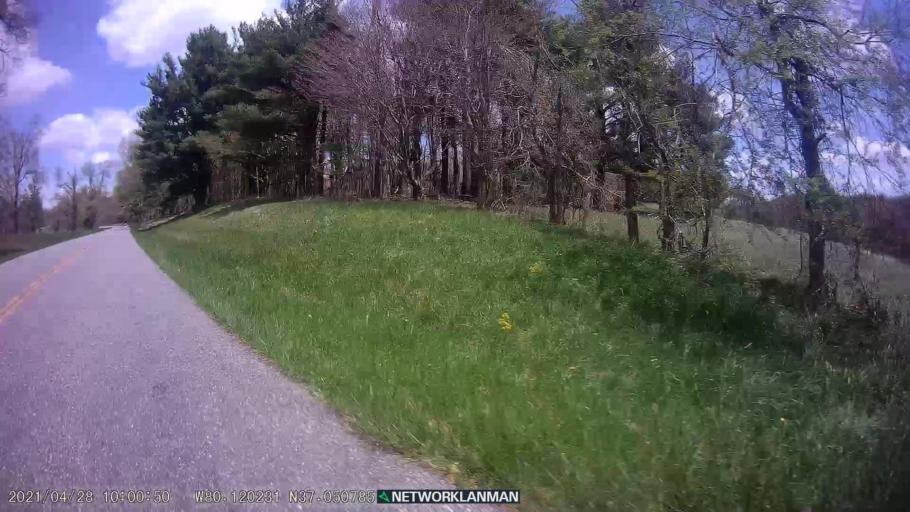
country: US
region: Virginia
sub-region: Franklin County
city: Ferrum
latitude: 37.0511
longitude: -80.1204
